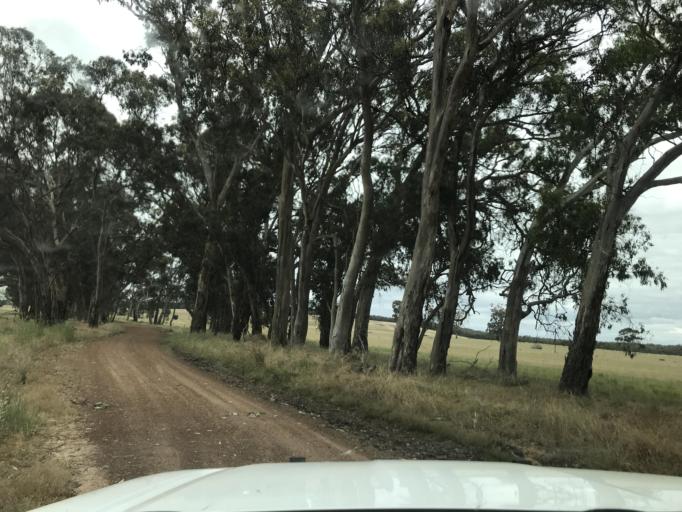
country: AU
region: South Australia
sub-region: Naracoorte and Lucindale
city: Naracoorte
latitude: -36.9257
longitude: 141.3158
